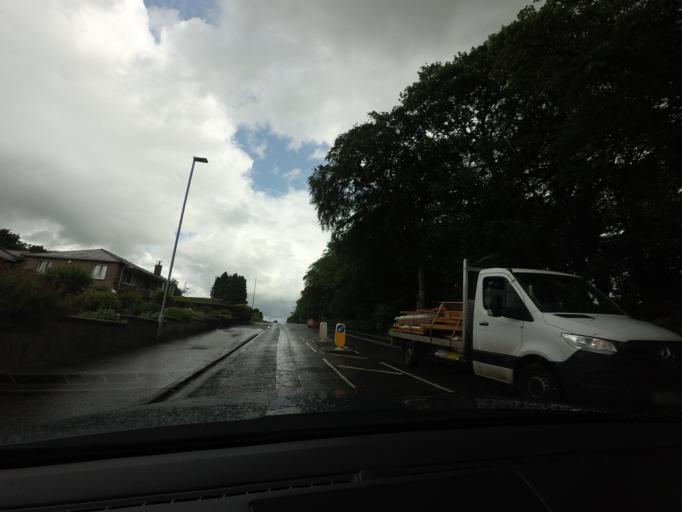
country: GB
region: Scotland
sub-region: Aberdeenshire
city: Turriff
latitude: 57.5410
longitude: -2.4521
